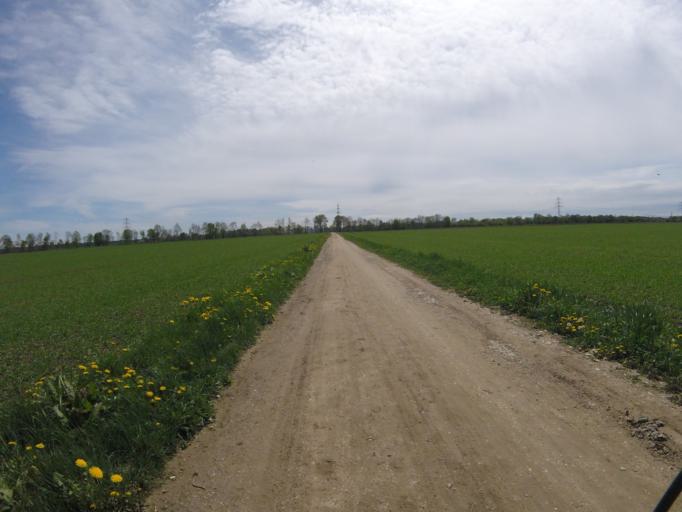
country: DE
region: Bavaria
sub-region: Upper Bavaria
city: Hohenbrunn
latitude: 48.0574
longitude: 11.6918
